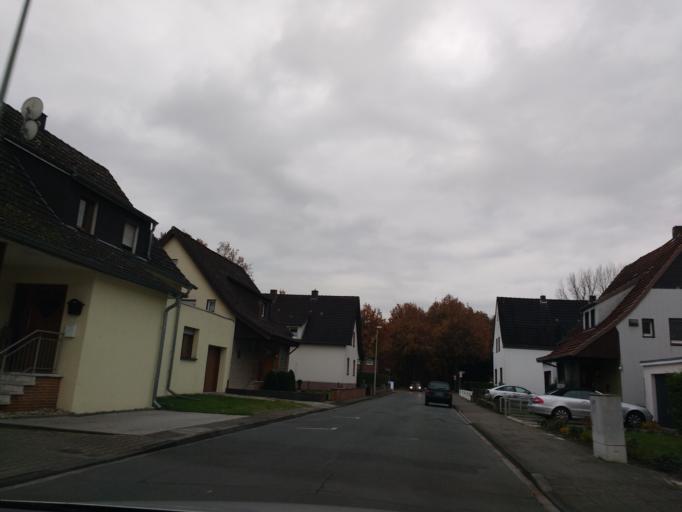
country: DE
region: North Rhine-Westphalia
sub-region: Regierungsbezirk Detmold
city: Paderborn
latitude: 51.7672
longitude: 8.7134
